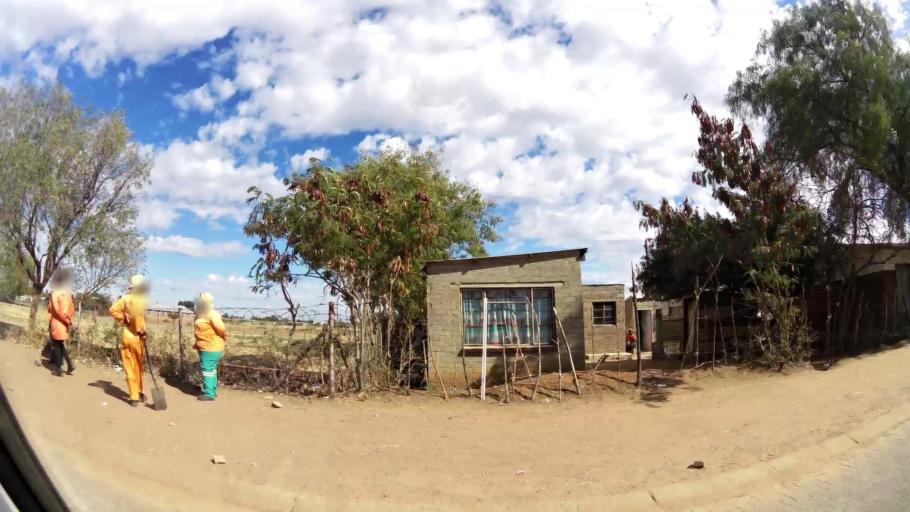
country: ZA
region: Limpopo
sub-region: Waterberg District Municipality
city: Bela-Bela
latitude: -24.8830
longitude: 28.3166
